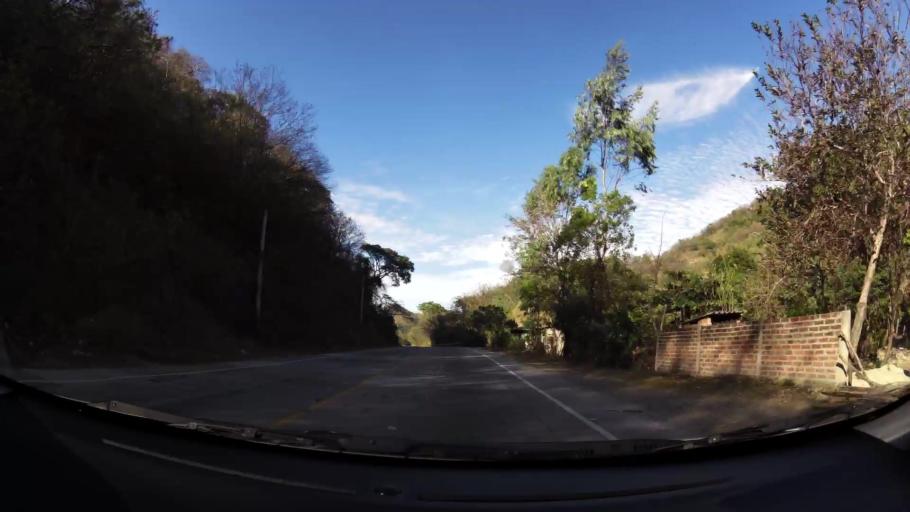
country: SV
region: Santa Ana
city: Texistepeque
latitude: 14.1495
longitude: -89.5145
